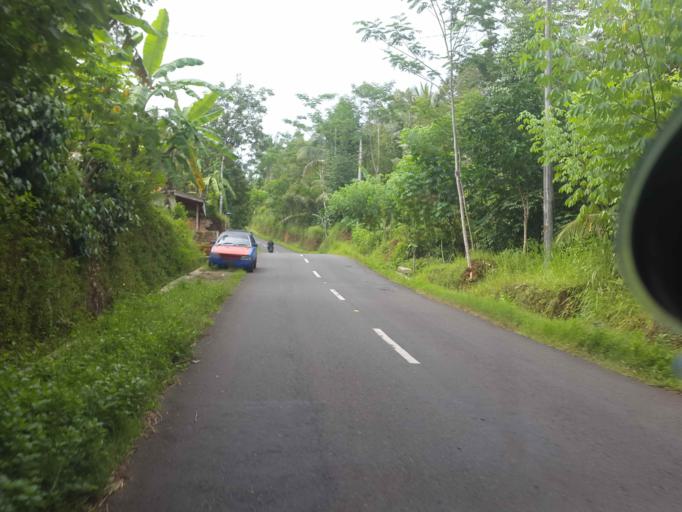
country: ID
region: Central Java
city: Banyumas
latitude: -7.5802
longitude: 109.3159
